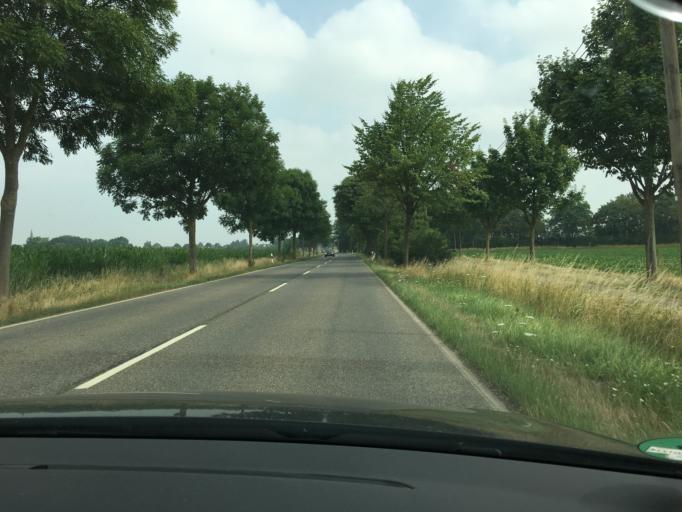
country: DE
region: North Rhine-Westphalia
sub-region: Regierungsbezirk Koln
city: Norvenich
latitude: 50.8030
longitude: 6.5867
